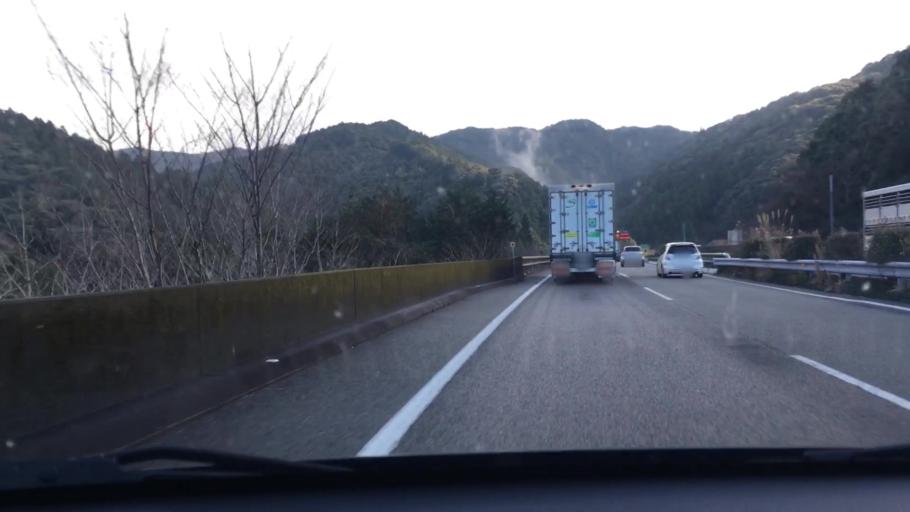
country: JP
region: Kumamoto
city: Hitoyoshi
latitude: 32.1380
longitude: 130.8022
